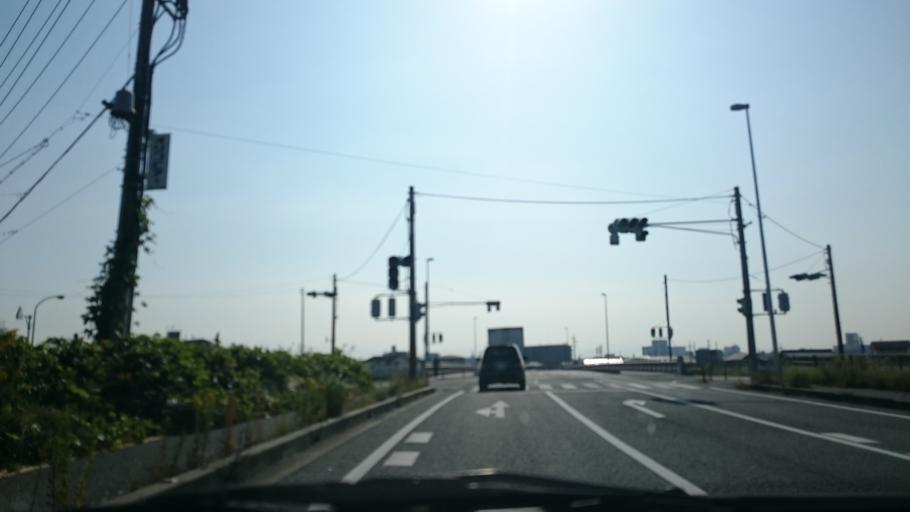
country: JP
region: Mie
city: Yokkaichi
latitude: 34.9814
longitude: 136.6209
